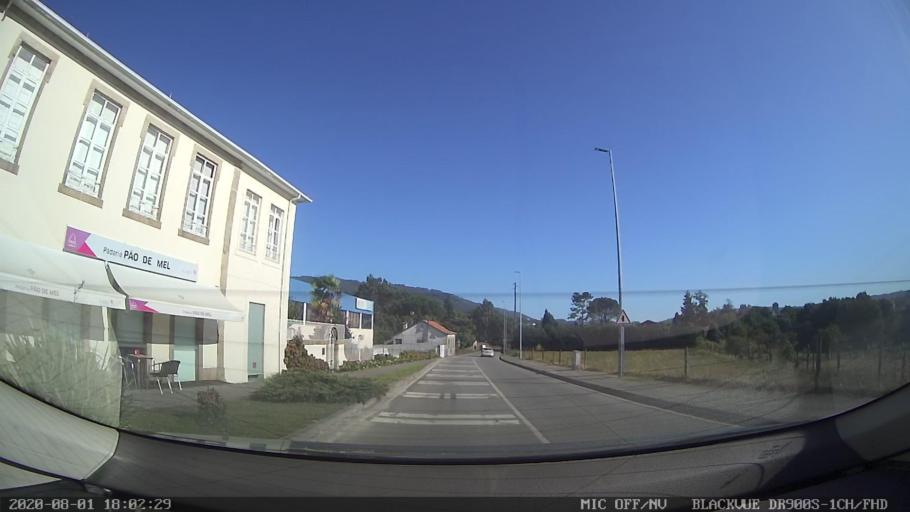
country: PT
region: Porto
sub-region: Santo Tirso
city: Santo Tirso
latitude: 41.3524
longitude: -8.4669
